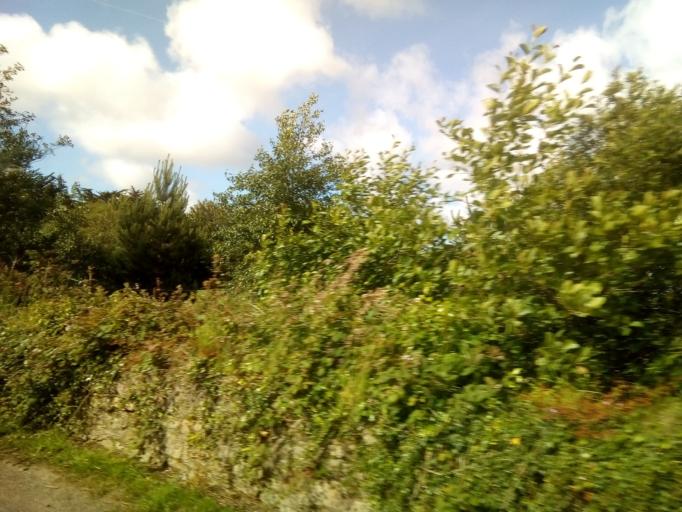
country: IE
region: Leinster
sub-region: Loch Garman
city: Loch Garman
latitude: 52.2618
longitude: -6.5568
